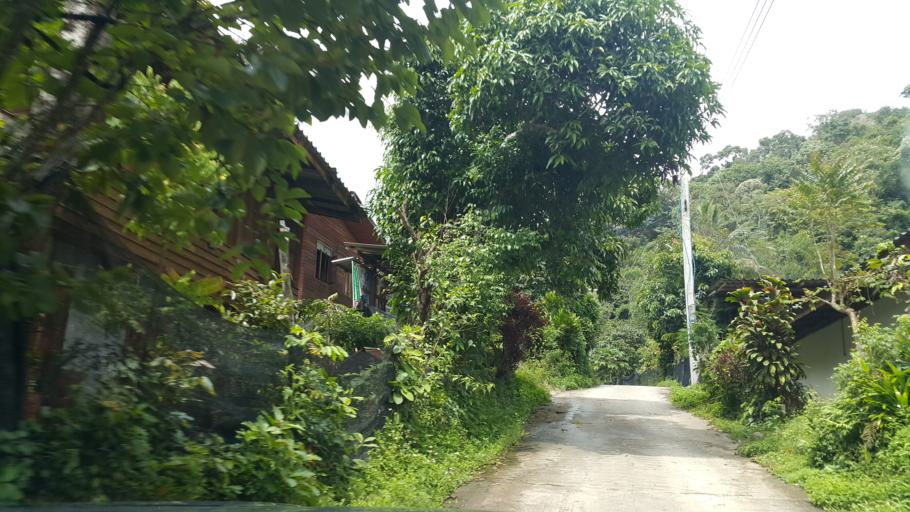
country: TH
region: Lampang
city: Wang Nuea
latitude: 19.0901
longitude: 99.3719
